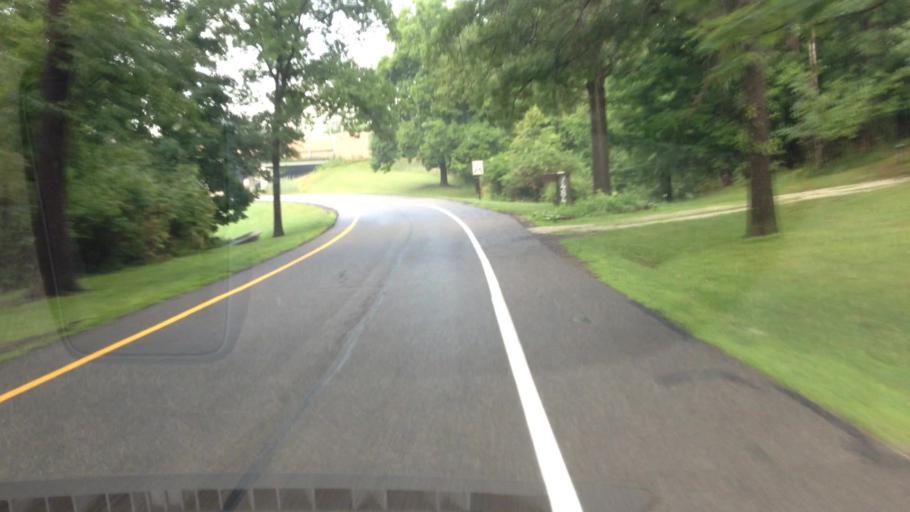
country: US
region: Ohio
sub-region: Cuyahoga County
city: Middleburg Heights
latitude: 41.3631
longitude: -81.8191
